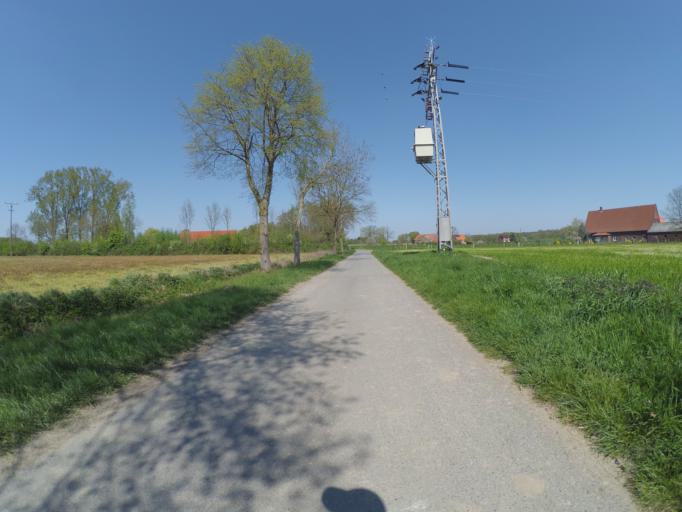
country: DE
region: North Rhine-Westphalia
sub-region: Regierungsbezirk Munster
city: Nordkirchen
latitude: 51.7618
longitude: 7.5489
